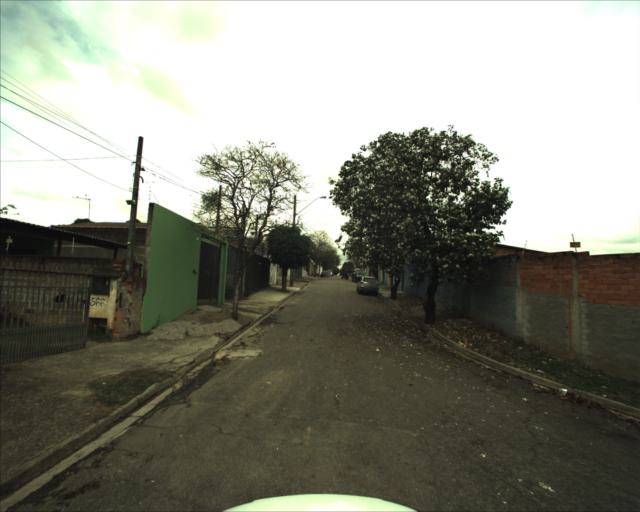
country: BR
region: Sao Paulo
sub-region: Sorocaba
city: Sorocaba
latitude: -23.4972
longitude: -47.4962
